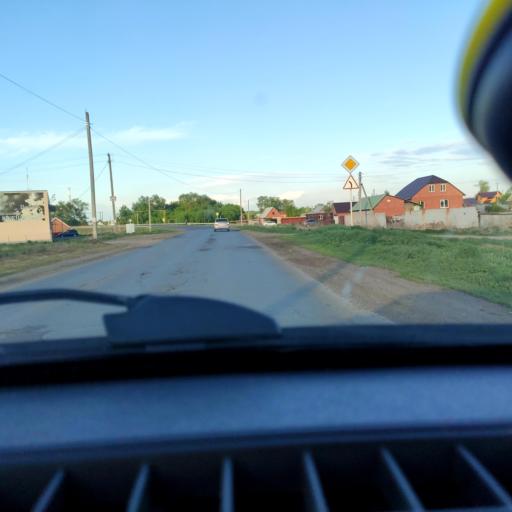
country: RU
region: Samara
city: Tol'yatti
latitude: 53.6814
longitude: 49.4264
